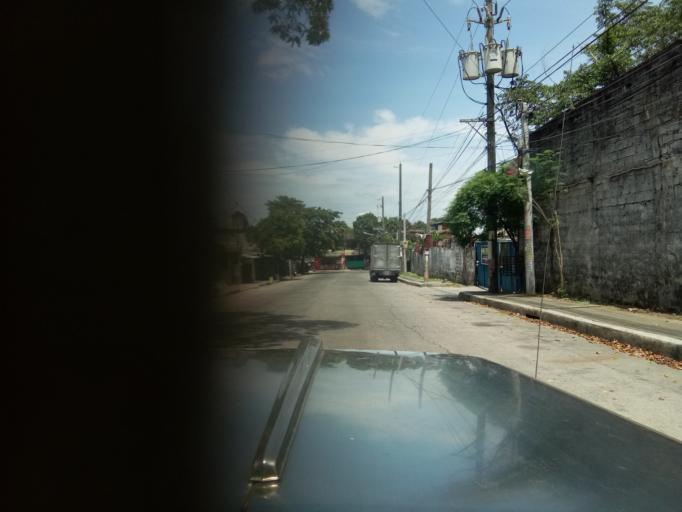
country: PH
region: Calabarzon
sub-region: Province of Cavite
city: Bulihan
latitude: 14.2882
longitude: 120.9979
